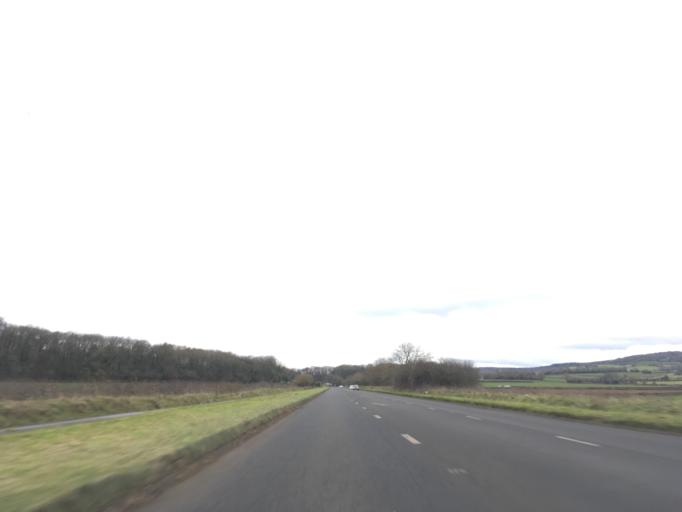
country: GB
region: Wales
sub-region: Monmouthshire
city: Rogiet
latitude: 51.6129
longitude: -2.7875
